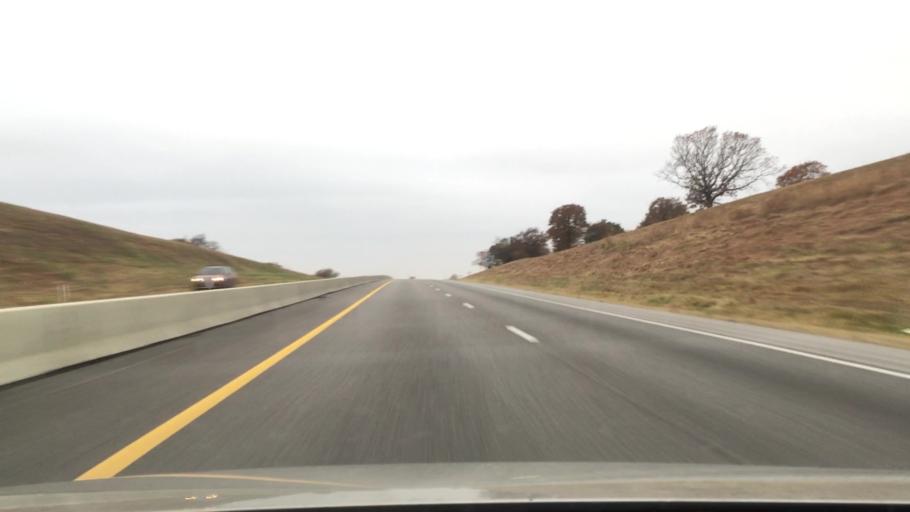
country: US
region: Oklahoma
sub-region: Lincoln County
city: Chandler
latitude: 35.7375
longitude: -96.7826
